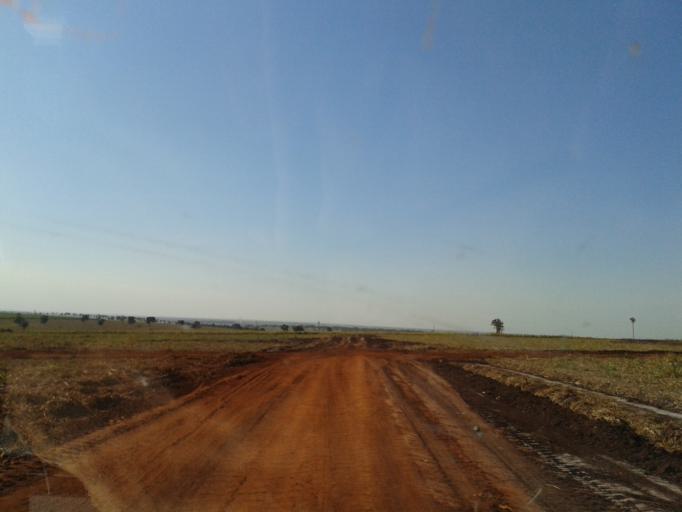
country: BR
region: Minas Gerais
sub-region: Santa Vitoria
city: Santa Vitoria
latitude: -18.7356
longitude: -50.2625
